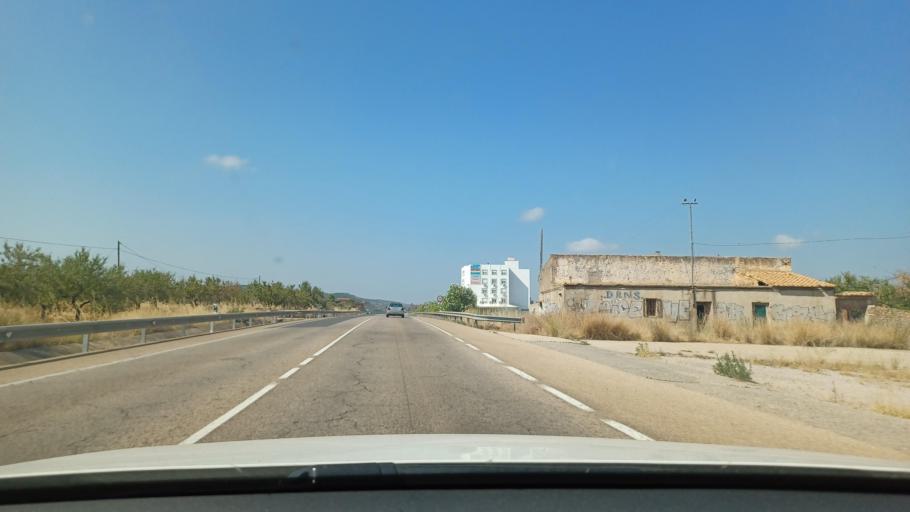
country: ES
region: Valencia
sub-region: Provincia de Castello
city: Torreblanca
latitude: 40.1923
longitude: 0.1747
